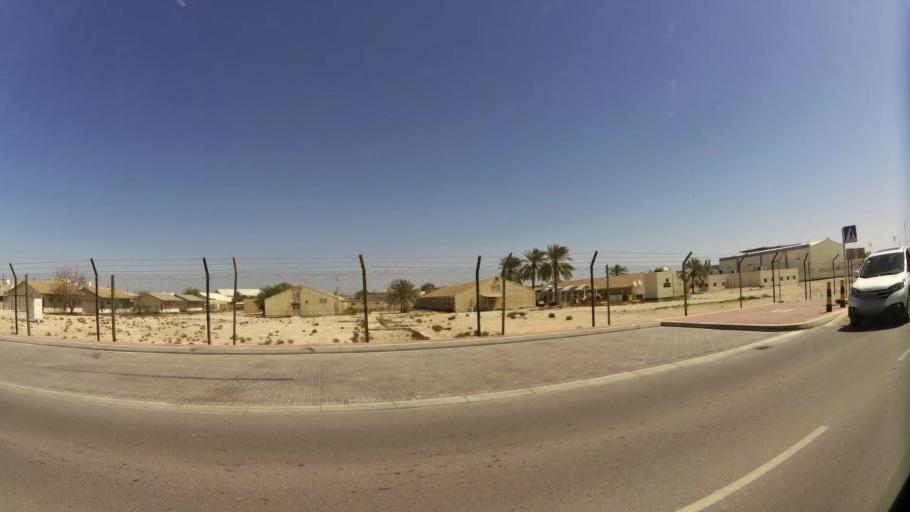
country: BH
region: Muharraq
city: Al Muharraq
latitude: 26.2692
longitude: 50.6128
